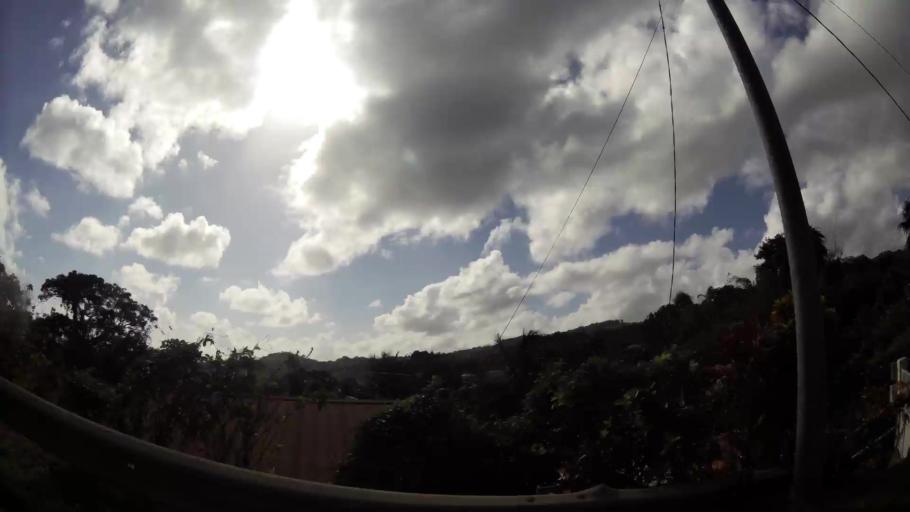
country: MQ
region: Martinique
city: Petite Riviere Salee
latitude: 14.7634
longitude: -60.9812
